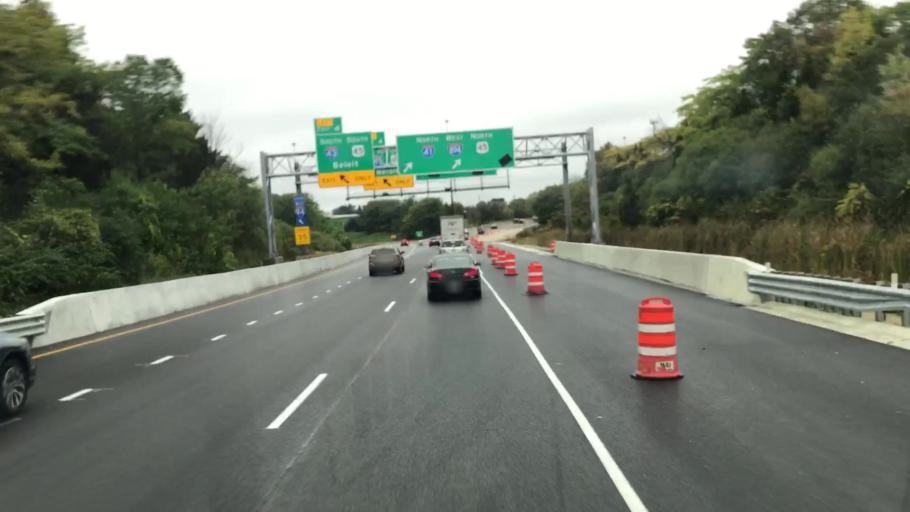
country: US
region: Wisconsin
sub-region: Milwaukee County
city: Greenfield
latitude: 42.9624
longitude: -88.0330
